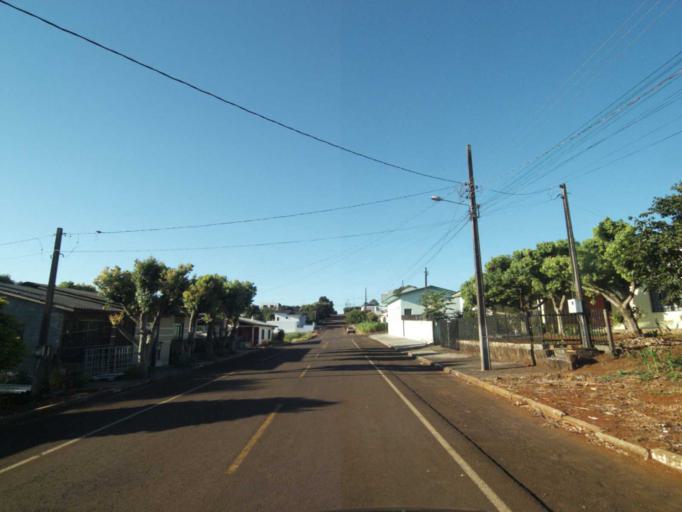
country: BR
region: Parana
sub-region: Coronel Vivida
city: Coronel Vivida
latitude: -25.9610
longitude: -52.8130
